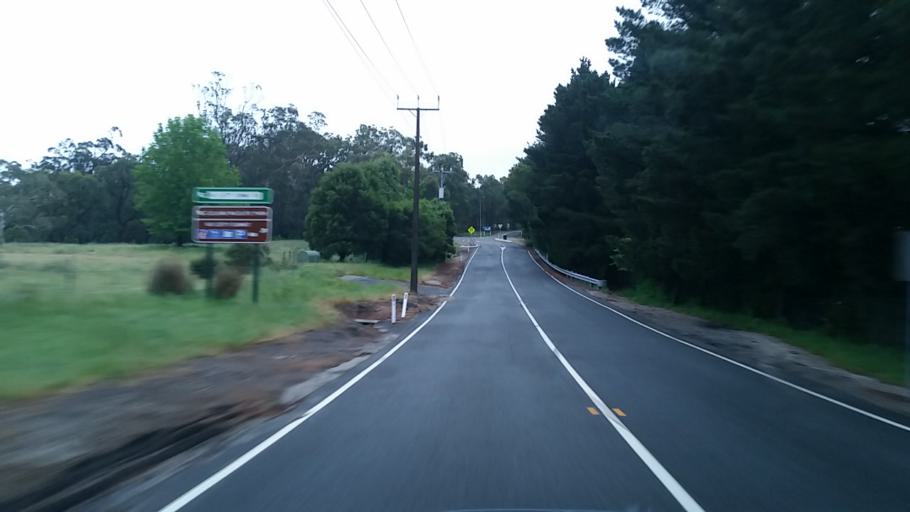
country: AU
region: South Australia
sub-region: Adelaide Hills
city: Crafers
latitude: -34.9782
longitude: 138.7093
